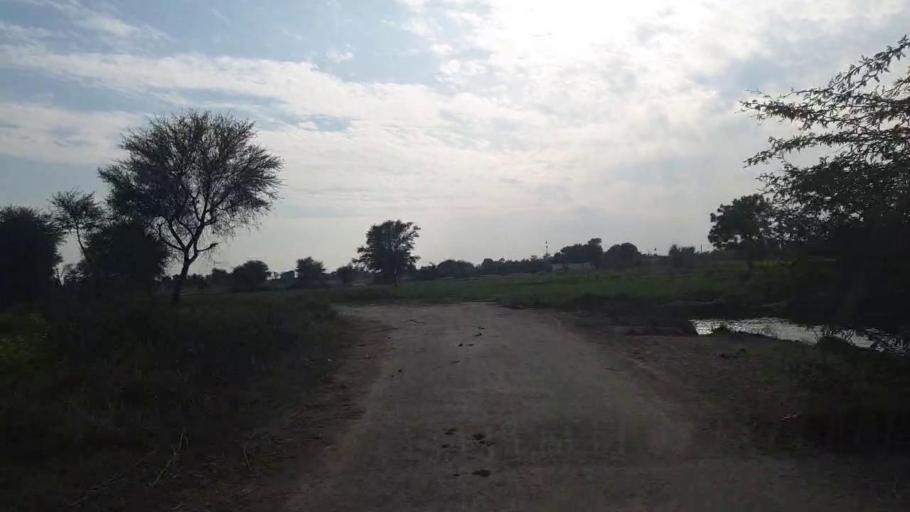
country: PK
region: Sindh
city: Shahpur Chakar
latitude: 26.0547
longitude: 68.5680
